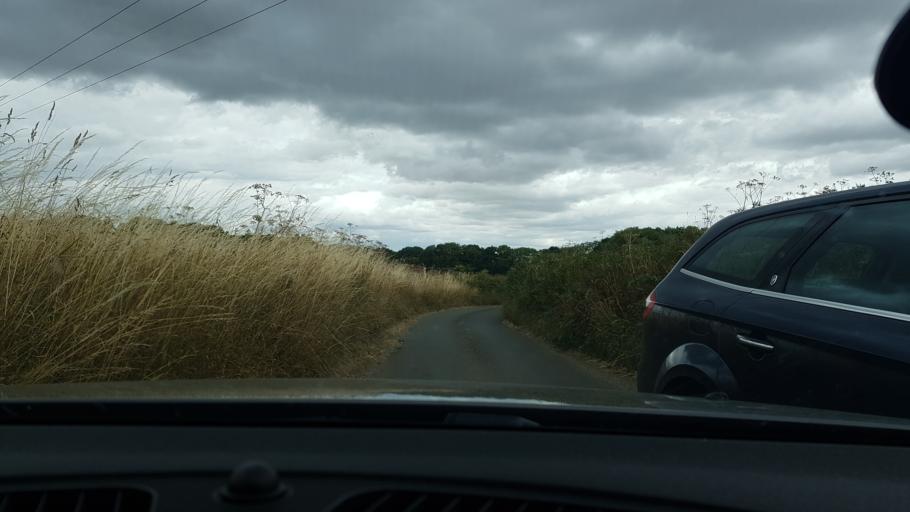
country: GB
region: England
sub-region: West Berkshire
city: Lambourn
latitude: 51.4732
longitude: -1.5081
